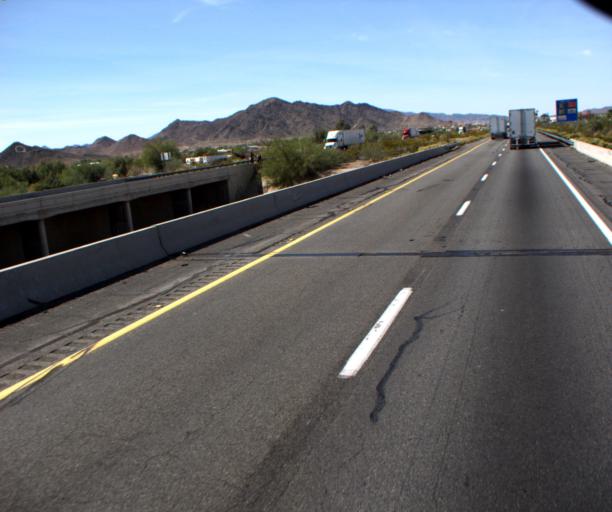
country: US
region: Arizona
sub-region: La Paz County
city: Quartzsite
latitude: 33.6627
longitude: -114.2214
